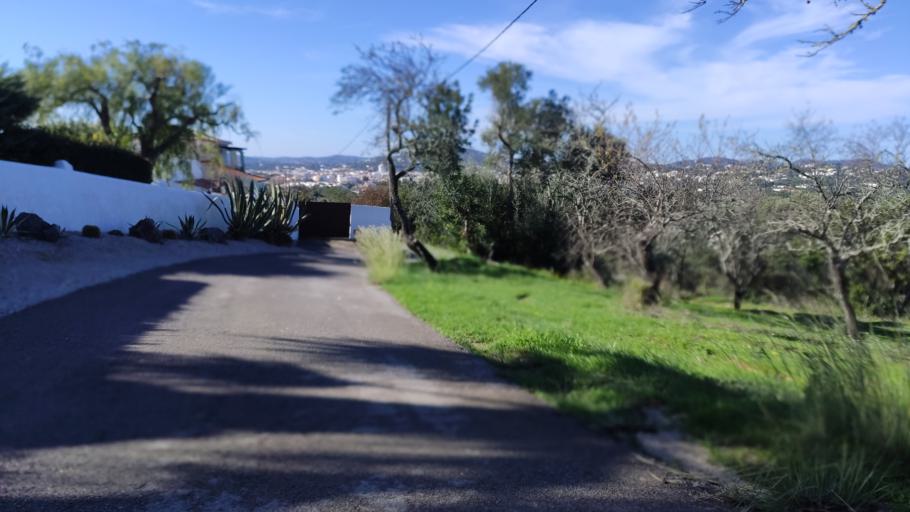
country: PT
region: Faro
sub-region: Sao Bras de Alportel
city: Sao Bras de Alportel
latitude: 37.1515
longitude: -7.8660
